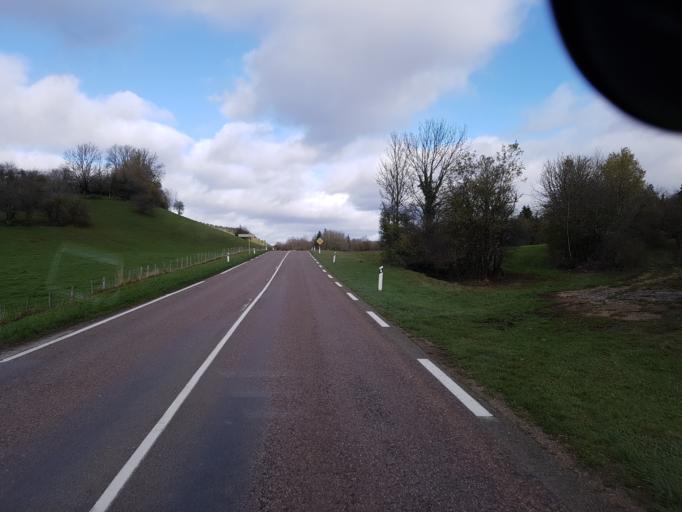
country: FR
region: Franche-Comte
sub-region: Departement du Jura
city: Champagnole
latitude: 46.6938
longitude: 5.9306
